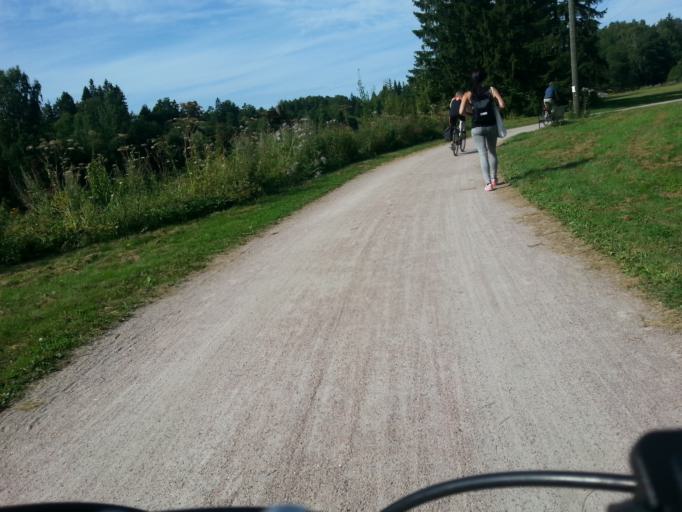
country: FI
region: Uusimaa
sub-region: Helsinki
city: Helsinki
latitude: 60.2253
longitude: 24.9843
